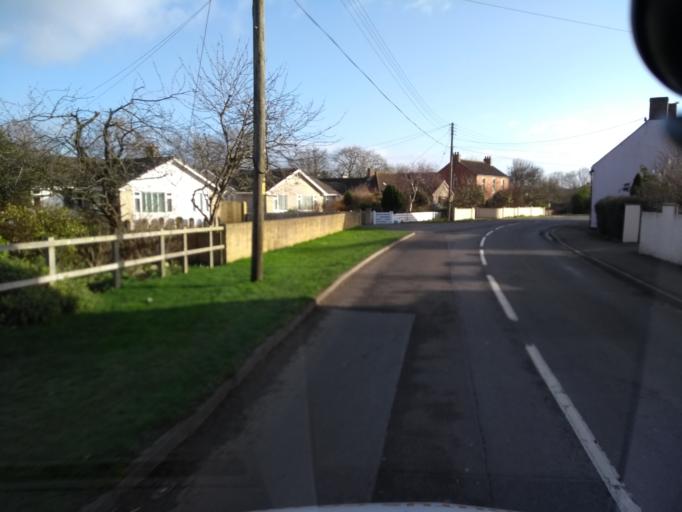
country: GB
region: England
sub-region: North Somerset
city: Bleadon
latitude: 51.2635
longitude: -2.9373
